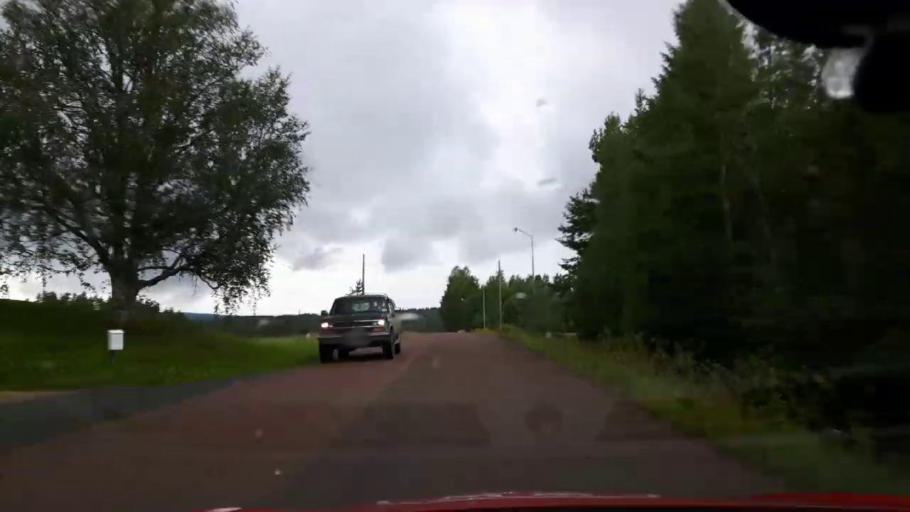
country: SE
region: Jaemtland
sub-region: Are Kommun
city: Jarpen
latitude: 63.3359
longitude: 13.7078
